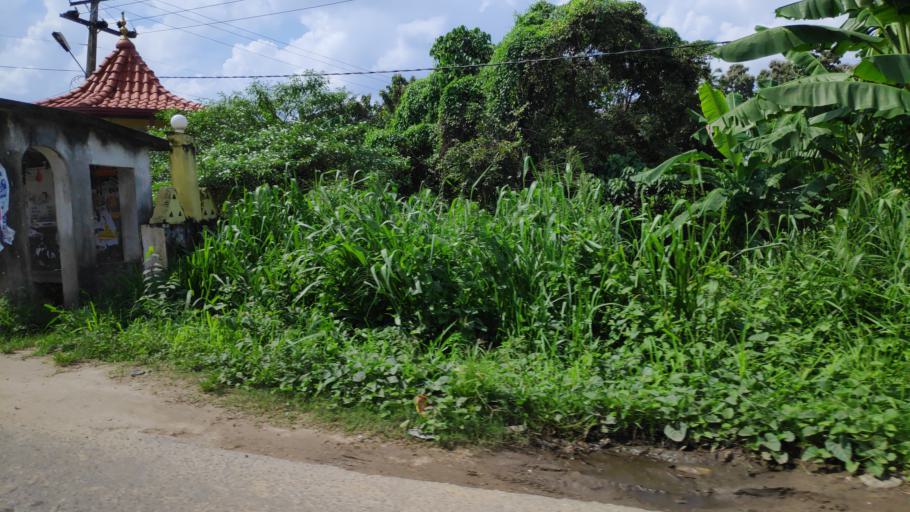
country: LK
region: Western
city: Minuwangoda
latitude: 7.2814
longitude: 80.0551
